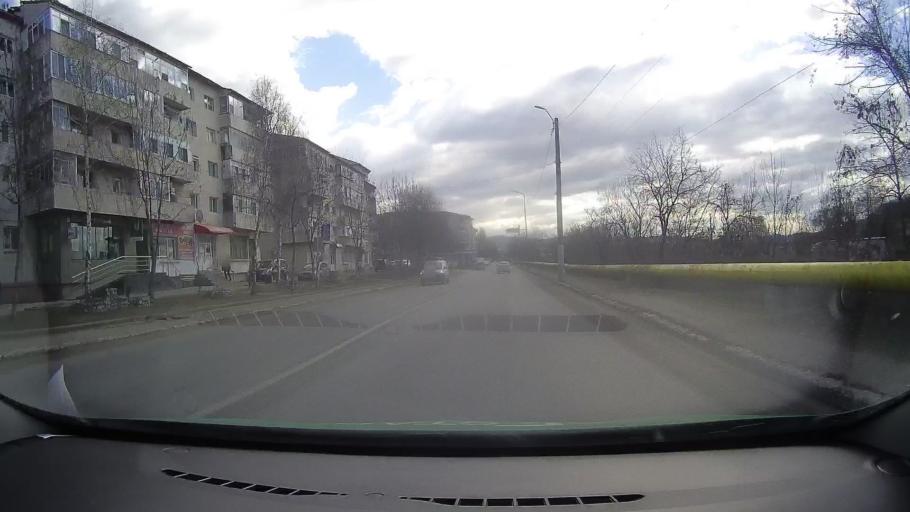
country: RO
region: Dambovita
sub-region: Oras Pucioasa
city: Pucioasa
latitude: 45.0792
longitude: 25.4286
